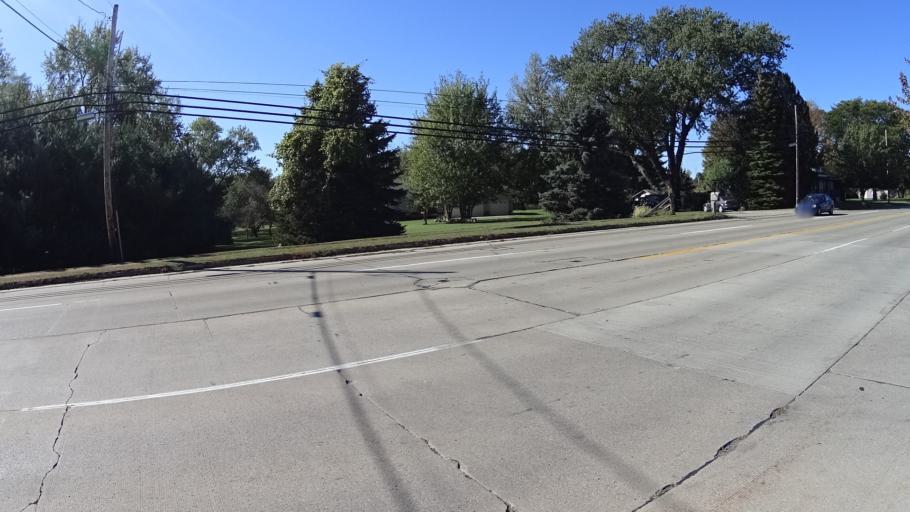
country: US
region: Ohio
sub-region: Lorain County
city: Sheffield
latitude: 41.4090
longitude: -82.1390
